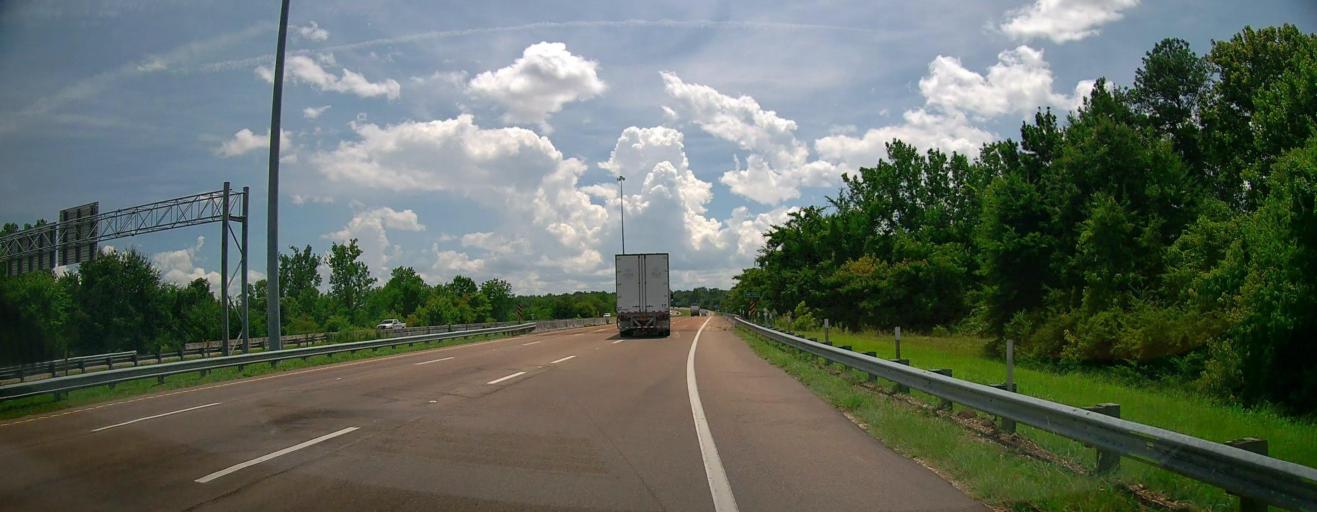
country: US
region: Mississippi
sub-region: Lee County
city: Tupelo
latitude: 34.2919
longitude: -88.7046
